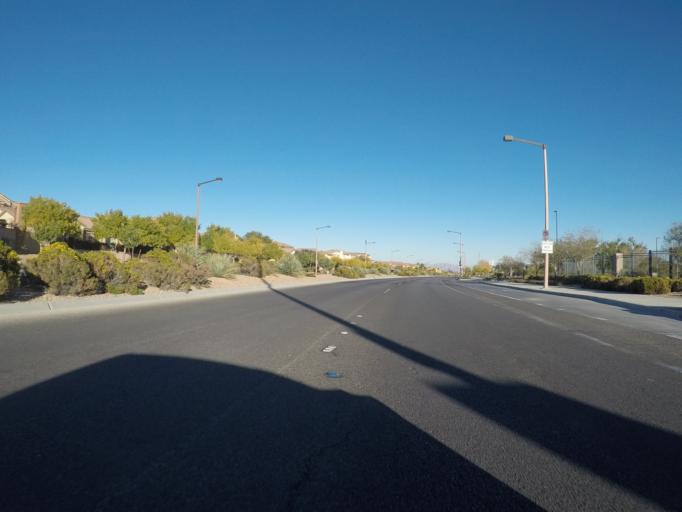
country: US
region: Nevada
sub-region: Clark County
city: Summerlin South
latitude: 36.1588
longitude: -115.3578
